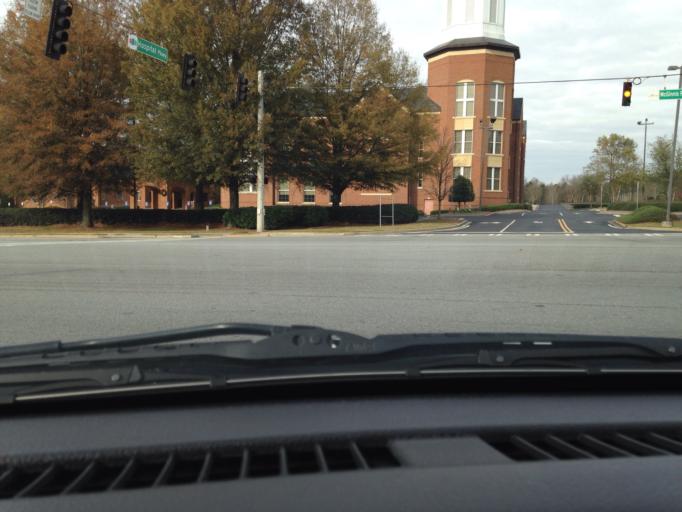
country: US
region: Georgia
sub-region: Fulton County
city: Johns Creek
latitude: 34.0690
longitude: -84.1752
